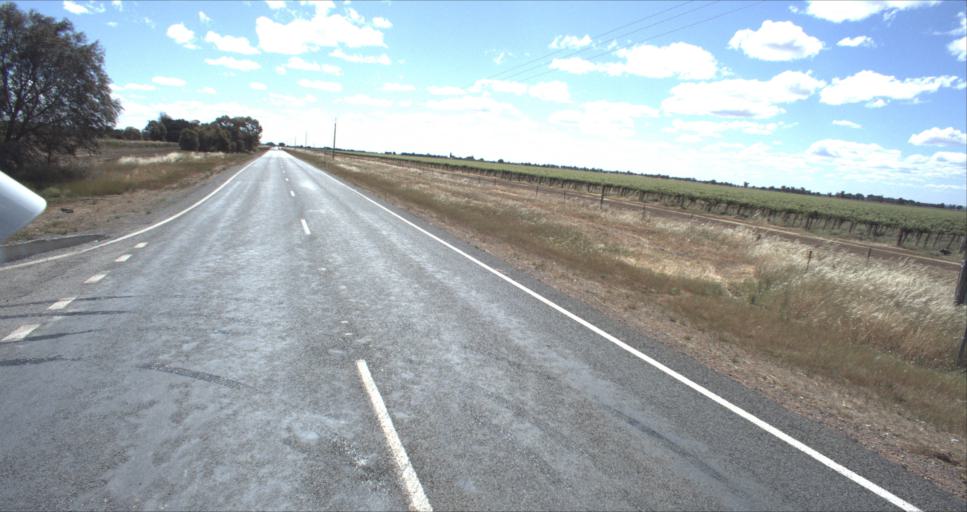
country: AU
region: New South Wales
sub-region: Leeton
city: Leeton
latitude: -34.5083
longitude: 146.2548
